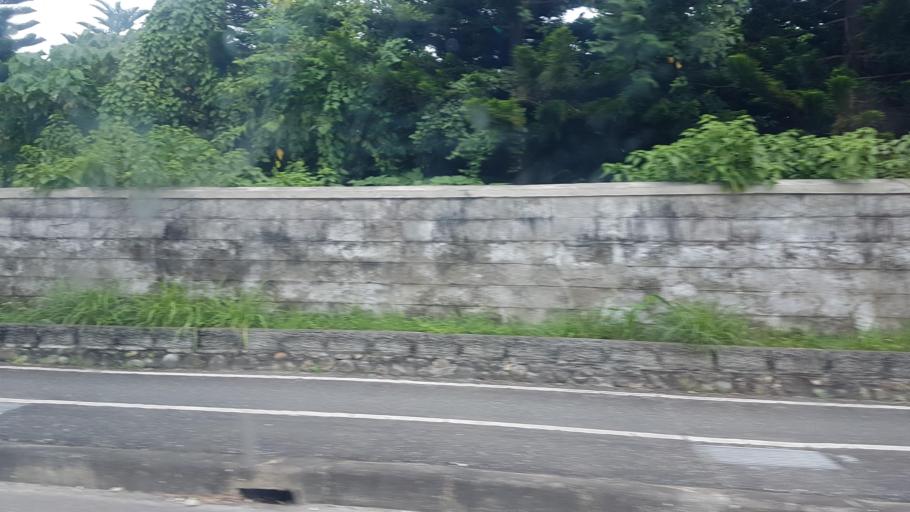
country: TW
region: Taiwan
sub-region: Hualien
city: Hualian
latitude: 24.0043
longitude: 121.6391
